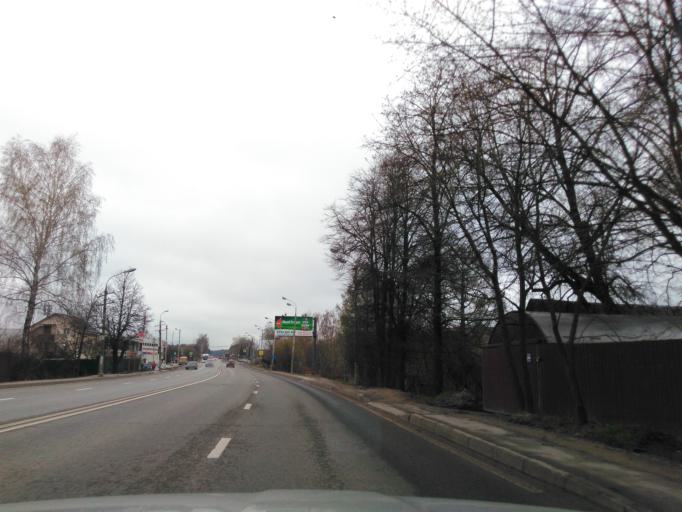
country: RU
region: Moskovskaya
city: Nakhabino
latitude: 55.8469
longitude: 37.1916
